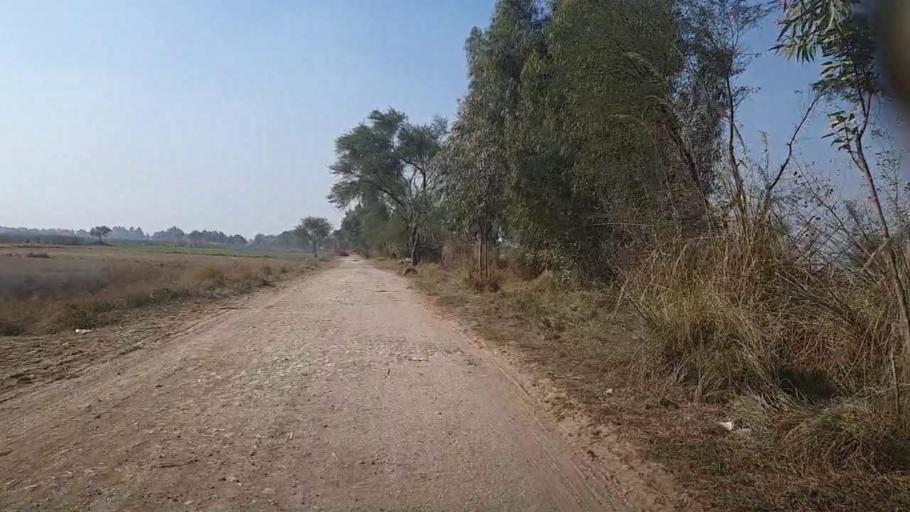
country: PK
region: Sindh
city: Mirpur Mathelo
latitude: 27.9021
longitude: 69.6337
